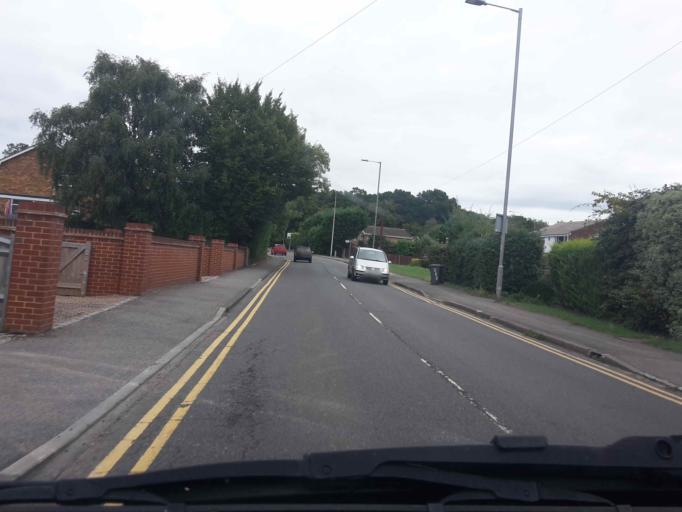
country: GB
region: England
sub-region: Reading
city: Reading
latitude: 51.4850
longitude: -0.9615
